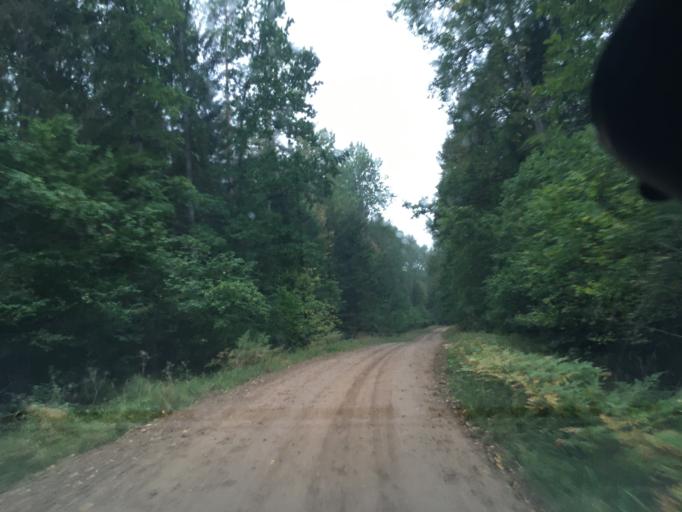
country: LV
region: Kuldigas Rajons
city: Kuldiga
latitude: 56.9850
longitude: 21.9961
